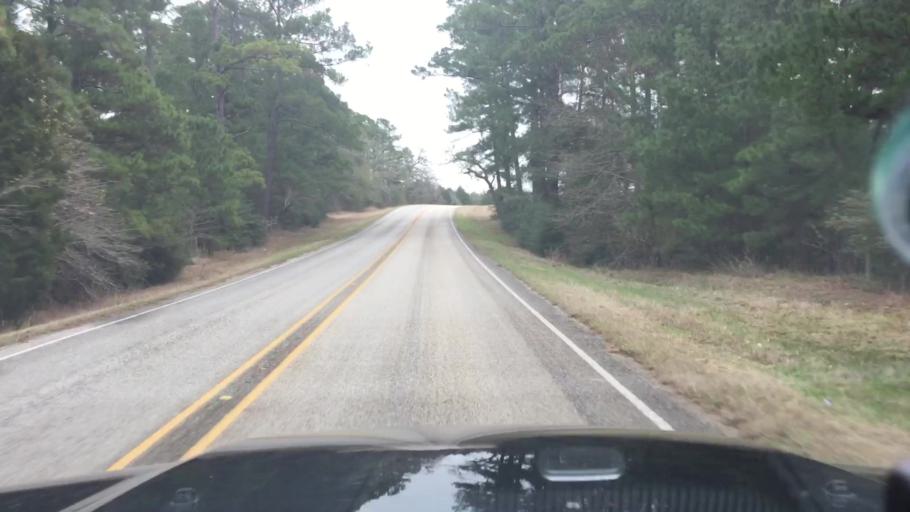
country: US
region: Texas
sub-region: Fayette County
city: La Grange
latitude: 30.0124
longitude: -96.9344
